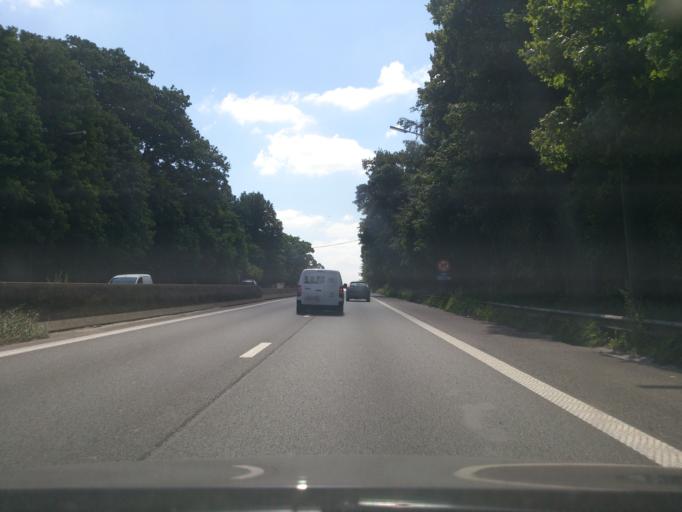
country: BE
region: Flanders
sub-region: Provincie Vlaams-Brabant
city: Hoeilaart
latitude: 50.7847
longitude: 4.4542
